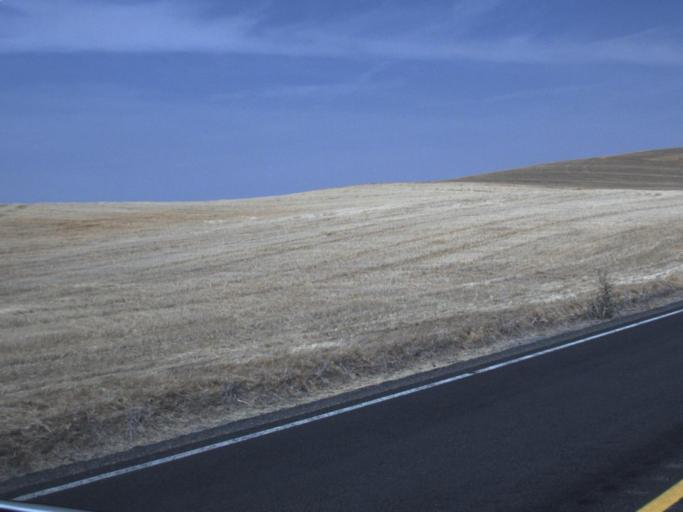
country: US
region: Washington
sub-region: Whitman County
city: Colfax
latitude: 47.1441
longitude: -117.2374
